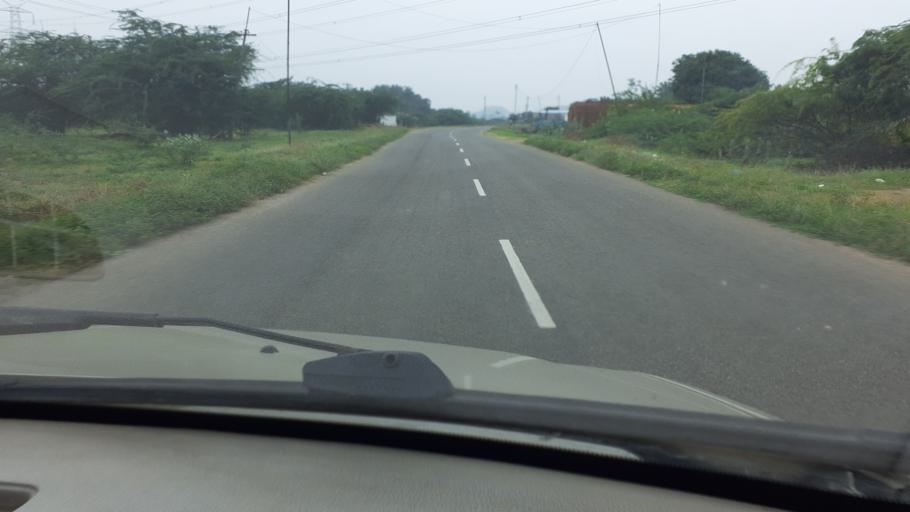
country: IN
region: Tamil Nadu
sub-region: Tirunelveli Kattabo
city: Nanguneri
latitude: 8.4872
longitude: 77.6465
